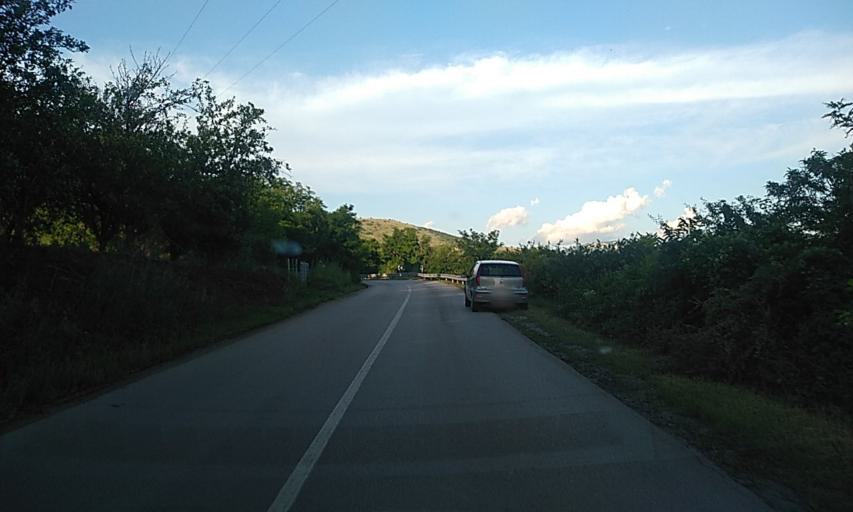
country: RS
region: Central Serbia
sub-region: Nisavski Okrug
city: Niska Banja
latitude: 43.3655
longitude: 21.9803
